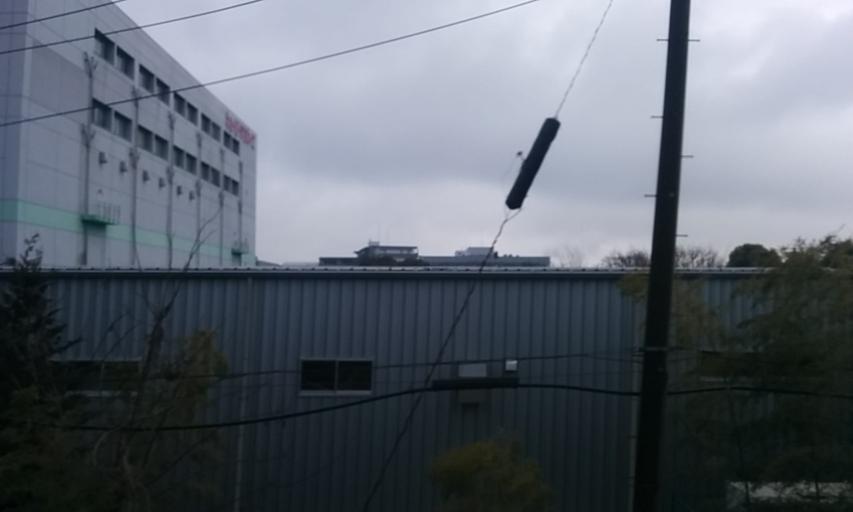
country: JP
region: Tokyo
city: Kokubunji
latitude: 35.6570
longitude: 139.4514
